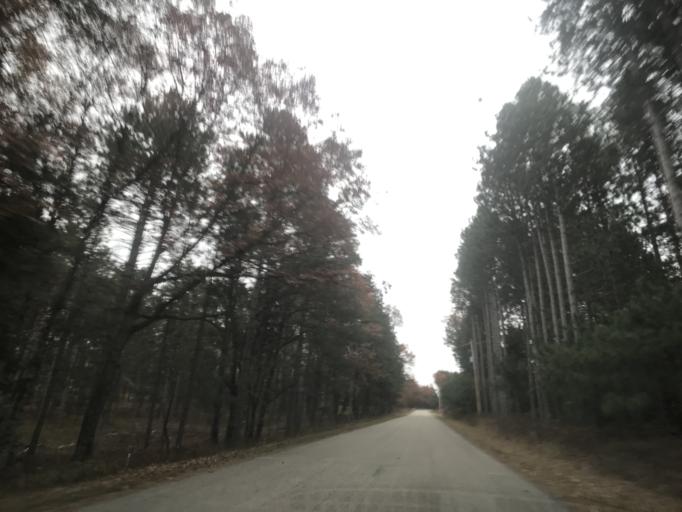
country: US
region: Wisconsin
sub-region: Oconto County
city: Gillett
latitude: 45.3108
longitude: -88.2736
